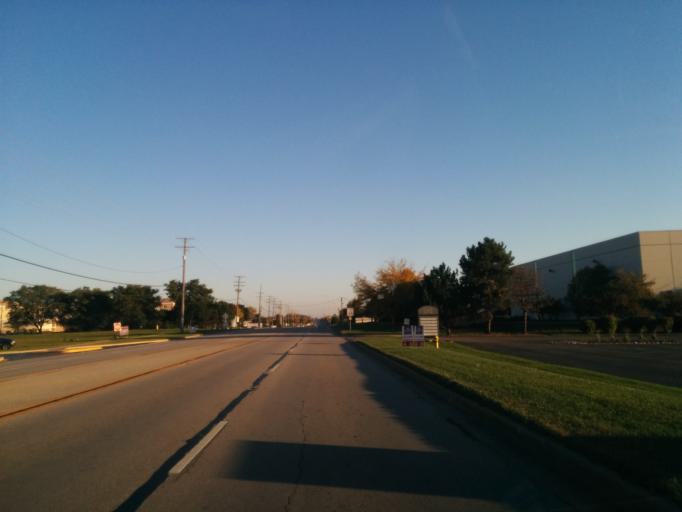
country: US
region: Illinois
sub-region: DuPage County
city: Carol Stream
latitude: 41.9001
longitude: -88.1205
